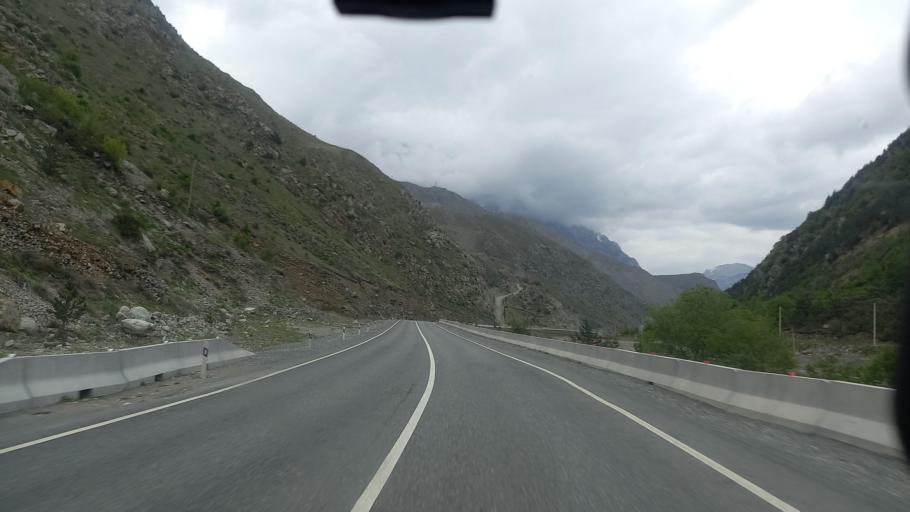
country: RU
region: North Ossetia
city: Mizur
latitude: 42.8410
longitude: 44.0329
